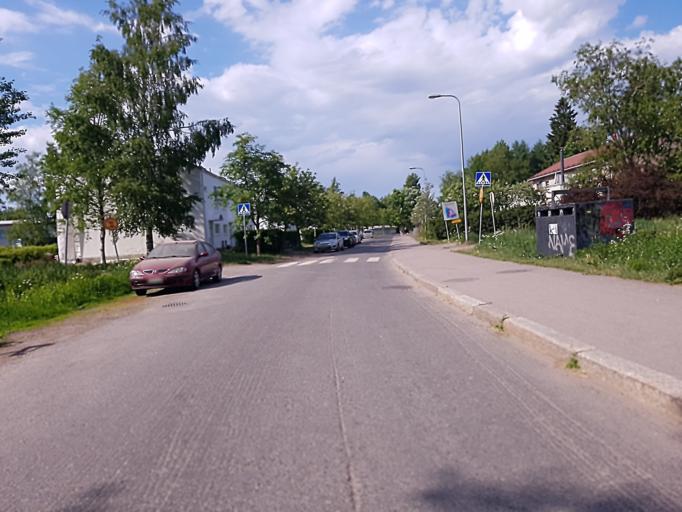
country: FI
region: Uusimaa
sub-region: Helsinki
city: Helsinki
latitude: 60.2235
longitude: 24.9607
